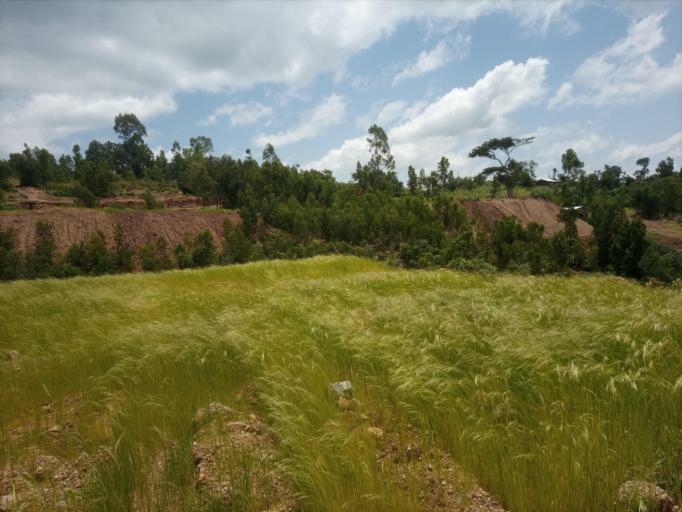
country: ET
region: Southern Nations, Nationalities, and People's Region
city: K'olito
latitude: 7.3079
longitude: 37.9664
